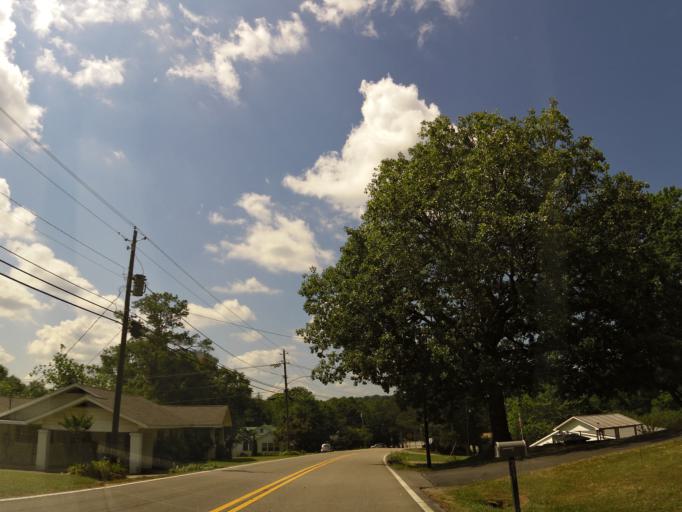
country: US
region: Alabama
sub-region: Marion County
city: Guin
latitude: 33.9685
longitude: -87.9077
